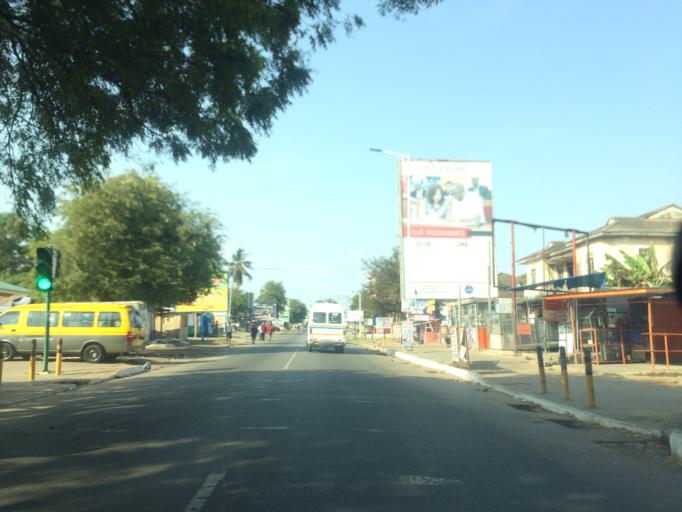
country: GH
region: Greater Accra
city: Accra
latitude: 5.5543
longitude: -0.1836
